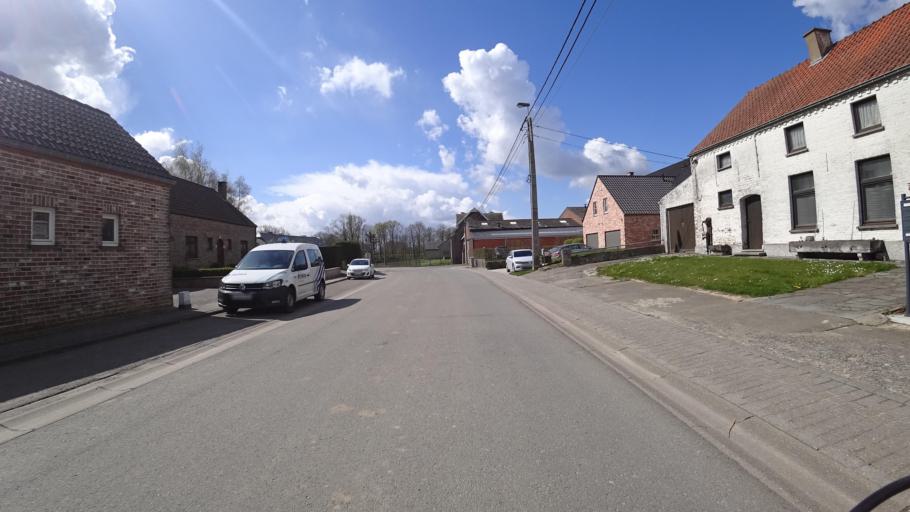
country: BE
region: Wallonia
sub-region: Province du Brabant Wallon
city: Chaumont-Gistoux
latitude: 50.6503
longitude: 4.7136
